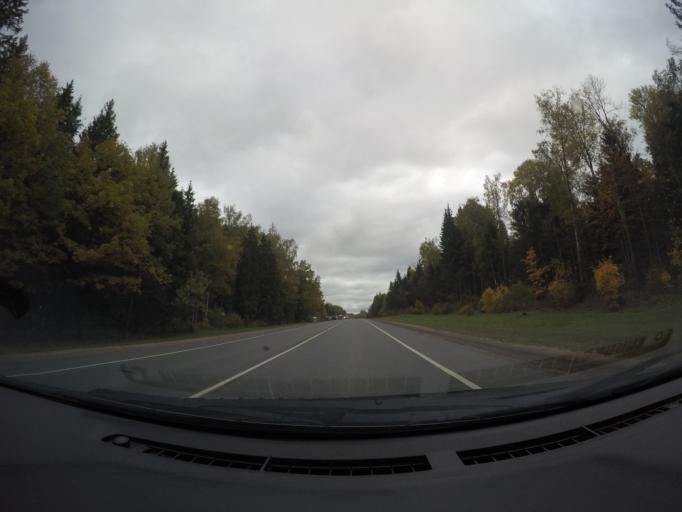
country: RU
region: Moskovskaya
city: Dorokhovo
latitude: 55.6038
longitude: 36.3565
